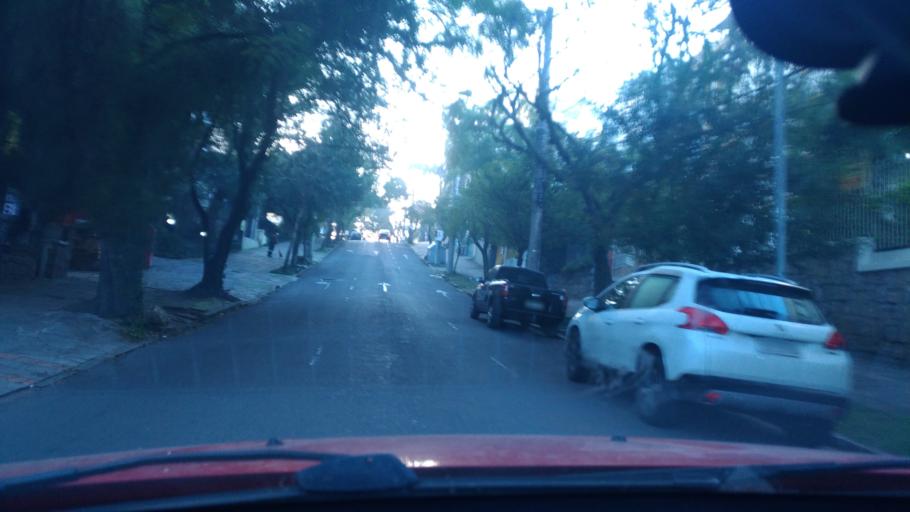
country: BR
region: Rio Grande do Sul
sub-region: Porto Alegre
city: Porto Alegre
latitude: -30.0275
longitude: -51.1959
